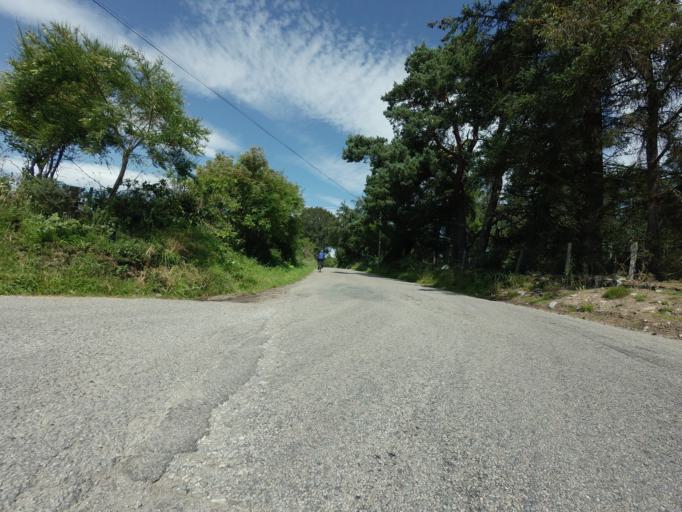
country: GB
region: Scotland
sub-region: Highland
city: Inverness
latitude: 57.5314
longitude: -4.3209
